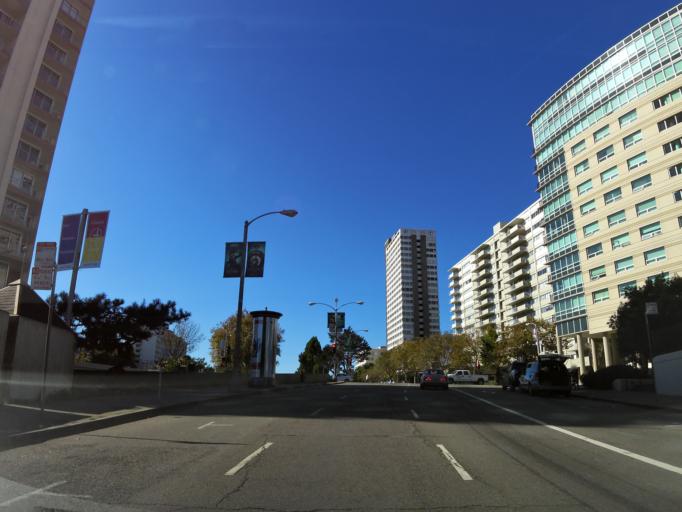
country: US
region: California
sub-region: San Francisco County
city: San Francisco
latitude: 37.7853
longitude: -122.4239
